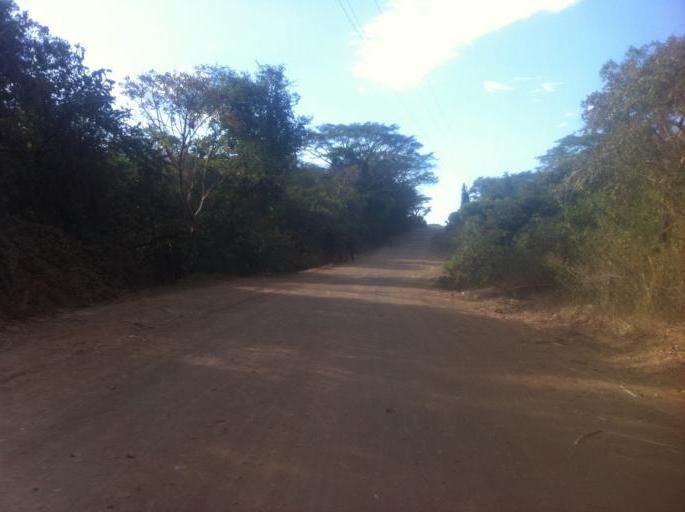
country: NI
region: Managua
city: Masachapa
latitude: 11.8344
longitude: -86.5104
